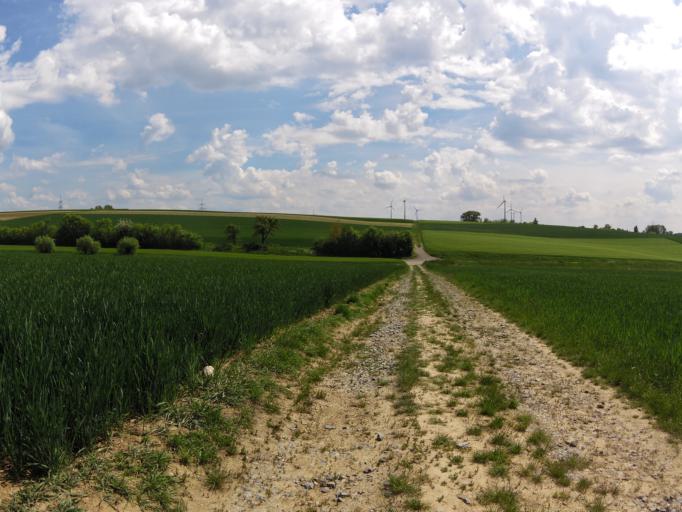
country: DE
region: Bavaria
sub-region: Regierungsbezirk Unterfranken
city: Theilheim
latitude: 49.7384
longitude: 10.0368
